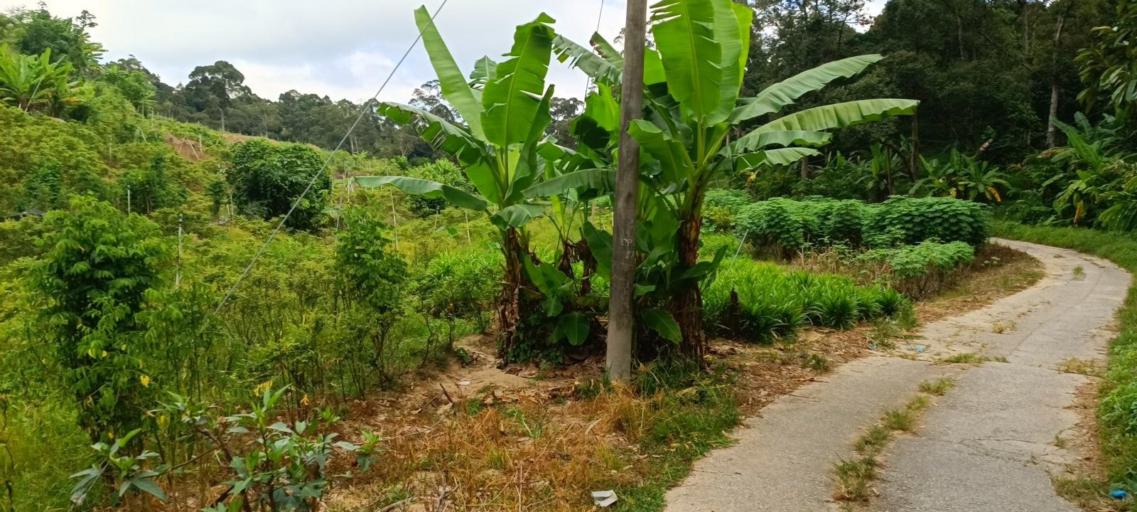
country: MY
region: Penang
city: Kampung Sungai Ara
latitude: 5.3340
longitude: 100.2547
